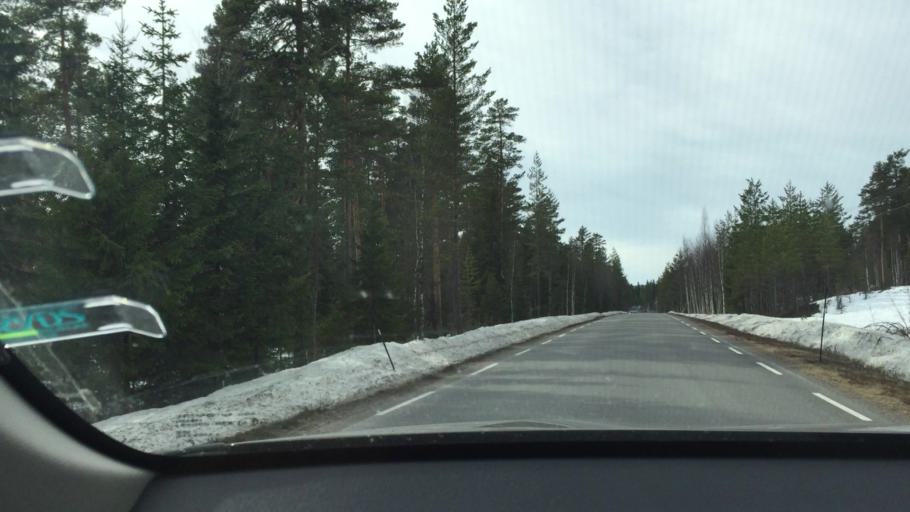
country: NO
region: Hedmark
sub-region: Trysil
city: Innbygda
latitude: 61.0646
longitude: 12.5913
